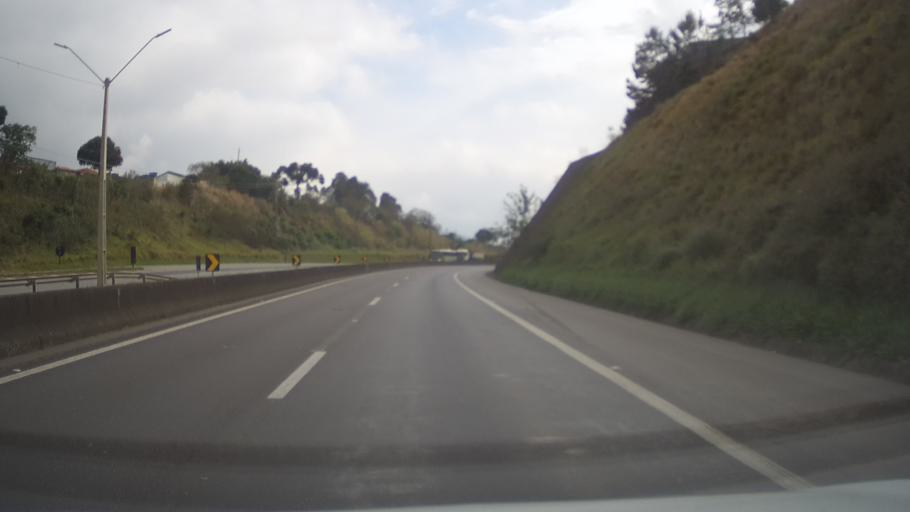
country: BR
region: Minas Gerais
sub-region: Extrema
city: Extrema
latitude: -22.8965
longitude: -46.4181
